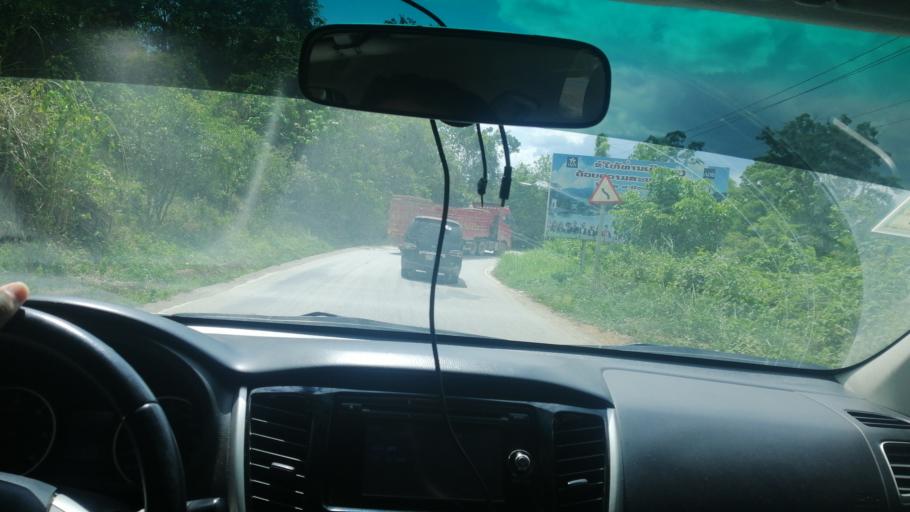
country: LA
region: Loungnamtha
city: Louang Namtha
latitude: 21.0418
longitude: 101.6503
